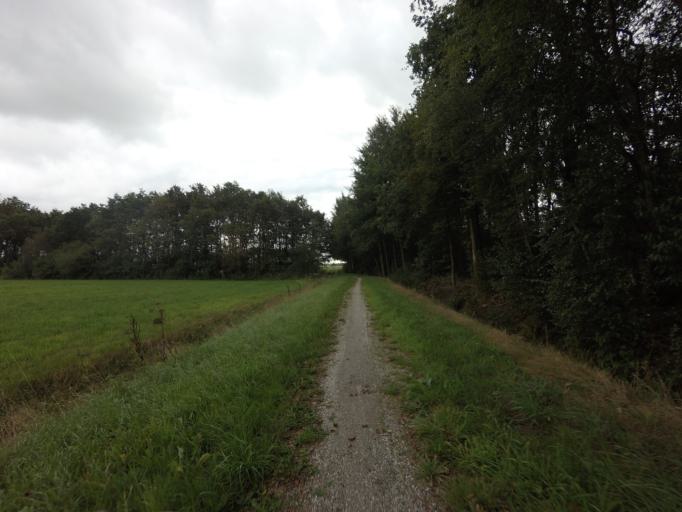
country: NL
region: Friesland
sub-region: Gemeente Weststellingwerf
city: Noordwolde
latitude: 52.9485
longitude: 6.1807
